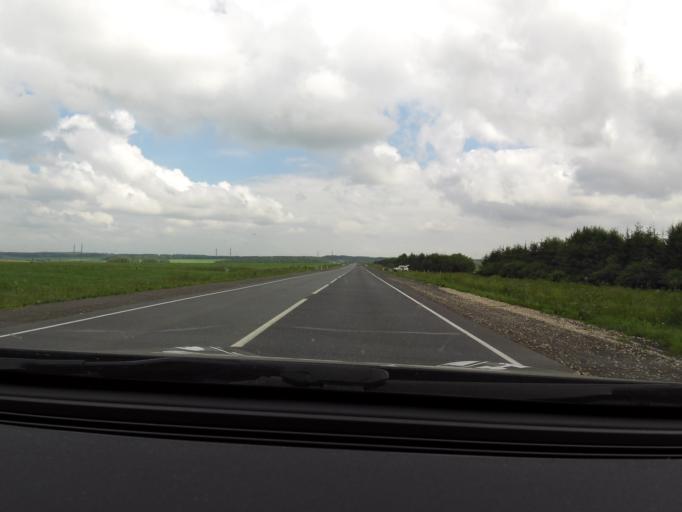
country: RU
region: Perm
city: Suksun
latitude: 57.1602
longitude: 57.1955
